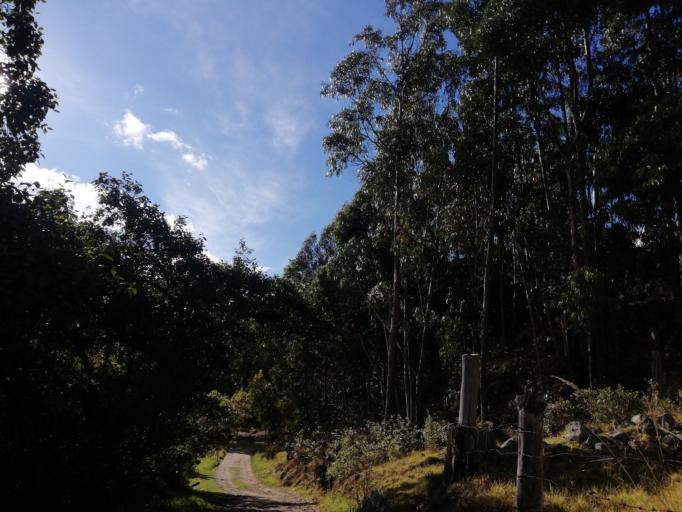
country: CO
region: Boyaca
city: Gameza
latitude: 5.8183
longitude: -72.8176
